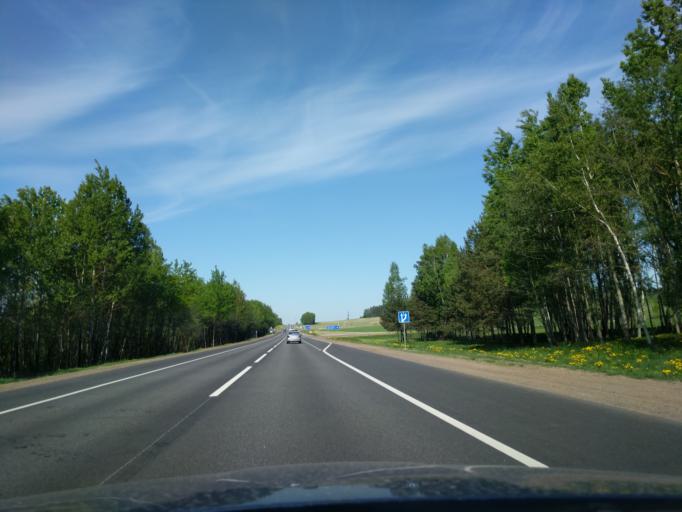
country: BY
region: Minsk
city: Bal'shavik
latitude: 54.0878
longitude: 27.5433
